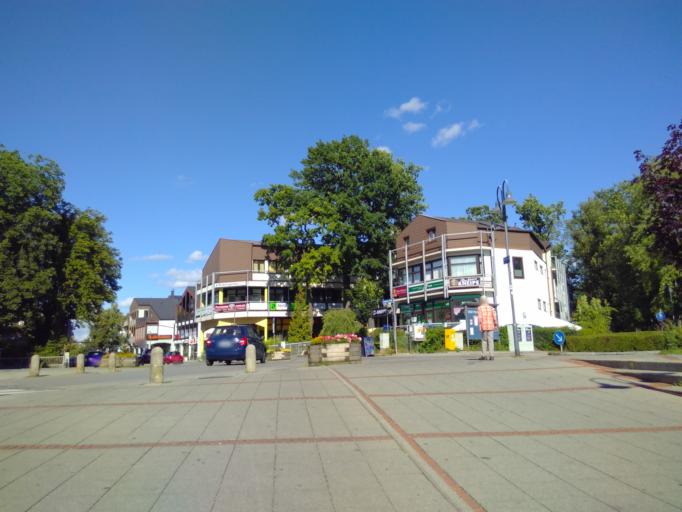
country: DE
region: Bavaria
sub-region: Upper Bavaria
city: Puchheim
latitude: 48.1727
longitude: 11.3530
